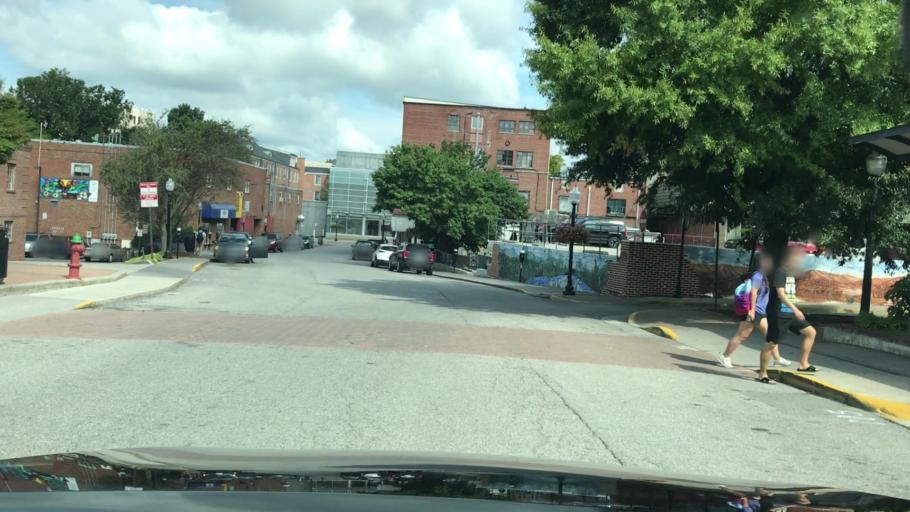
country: US
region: Virginia
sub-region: Montgomery County
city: Blacksburg
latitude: 37.2293
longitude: -80.4153
